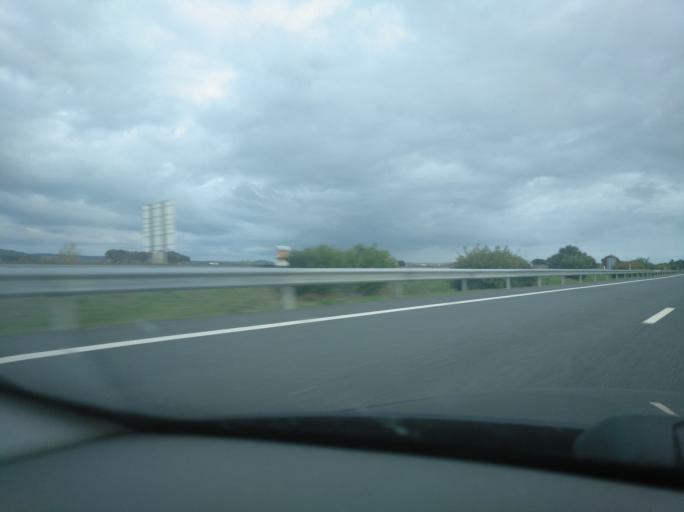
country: PT
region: Evora
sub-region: Montemor-O-Novo
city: Montemor-o-Novo
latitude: 38.6469
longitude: -8.1546
